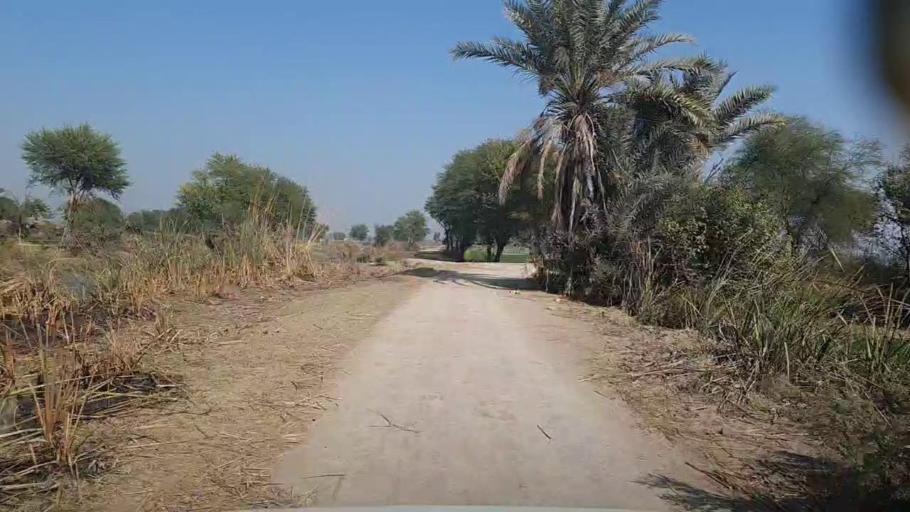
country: PK
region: Sindh
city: Khairpur
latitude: 27.9775
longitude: 69.7108
